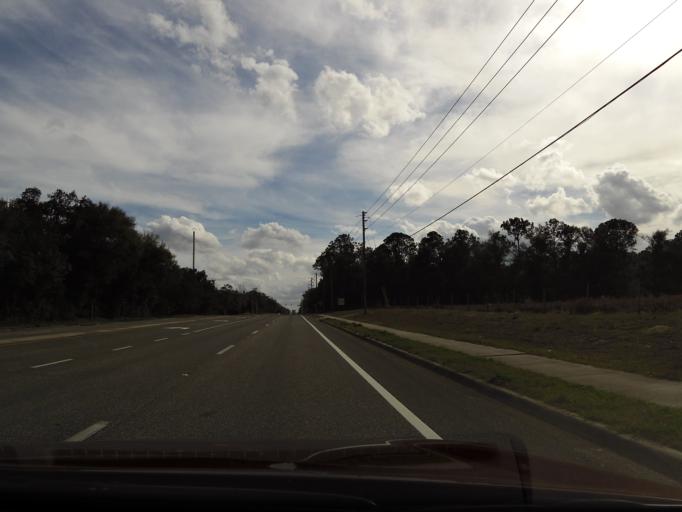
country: US
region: Florida
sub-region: Volusia County
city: North DeLand
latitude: 29.0748
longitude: -81.3256
